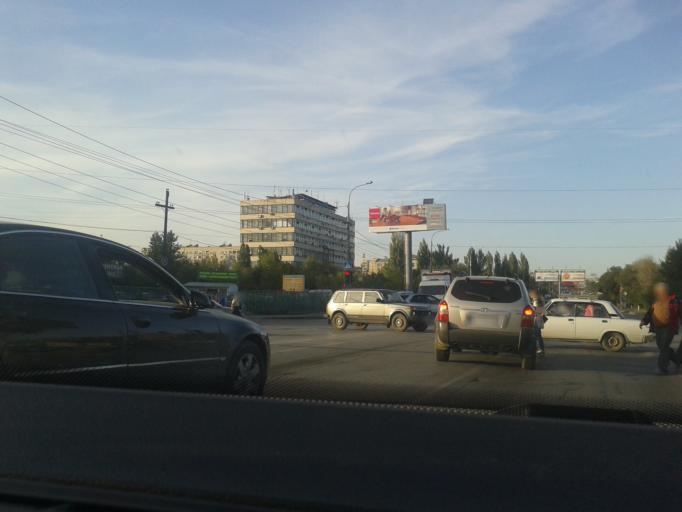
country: RU
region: Volgograd
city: Volgograd
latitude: 48.6549
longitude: 44.4368
